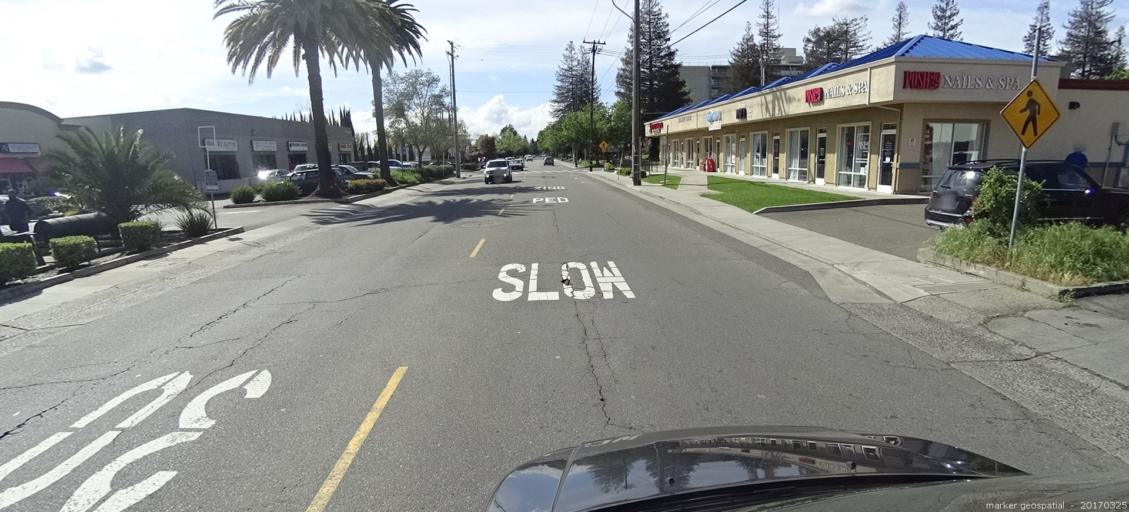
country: US
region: California
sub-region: Sacramento County
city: Parkway
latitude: 38.5468
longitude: -121.4383
